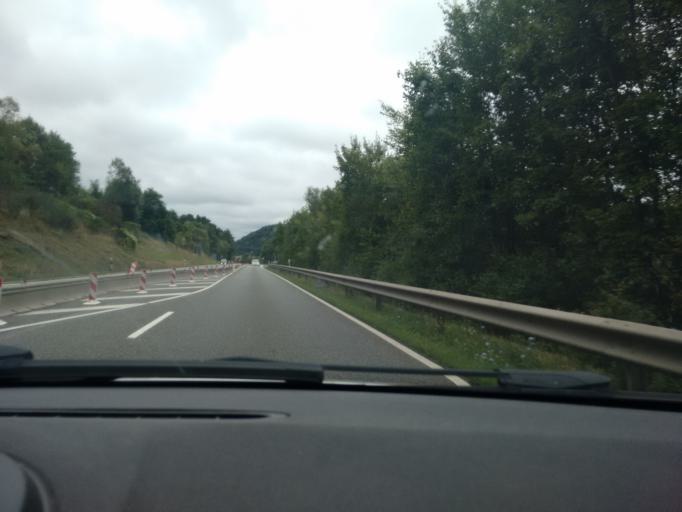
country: DE
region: Rheinland-Pfalz
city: Barenbach
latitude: 49.7623
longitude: 7.4416
